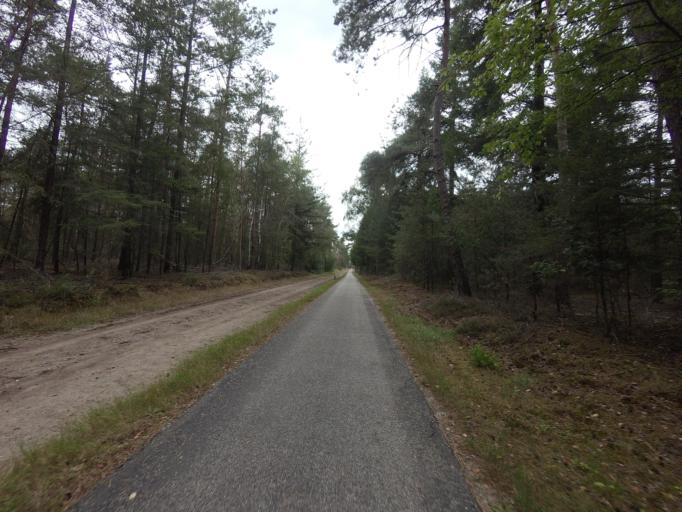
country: NL
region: Overijssel
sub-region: Gemeente Hof van Twente
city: Markelo
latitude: 52.3074
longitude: 6.4528
